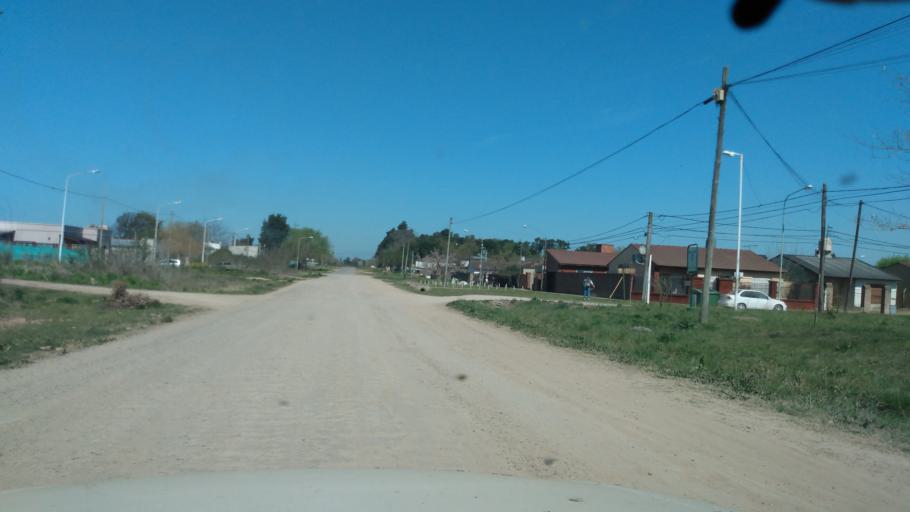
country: AR
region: Buenos Aires
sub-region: Partido de Lujan
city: Lujan
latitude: -34.5673
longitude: -59.1395
